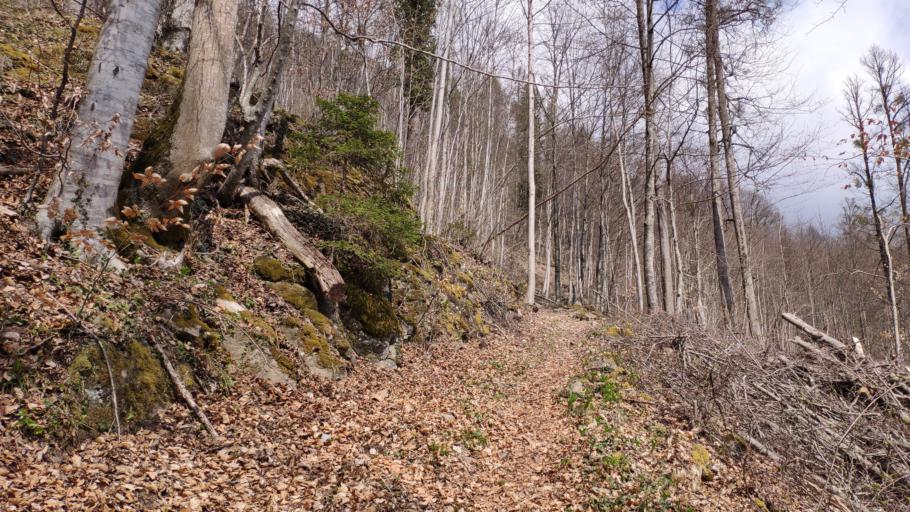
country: CH
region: Bern
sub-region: Interlaken-Oberhasli District
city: Brienz
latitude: 46.7457
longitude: 7.9727
